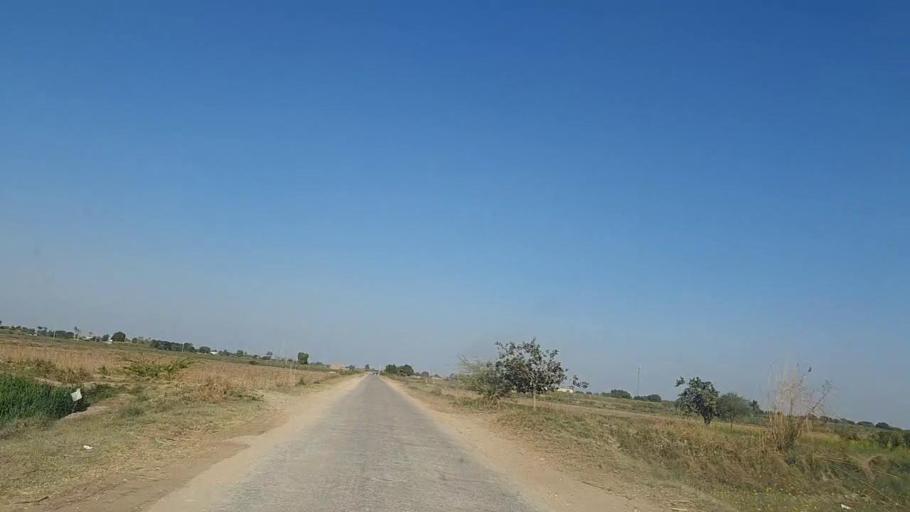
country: PK
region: Sindh
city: Digri
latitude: 25.1536
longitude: 69.0234
